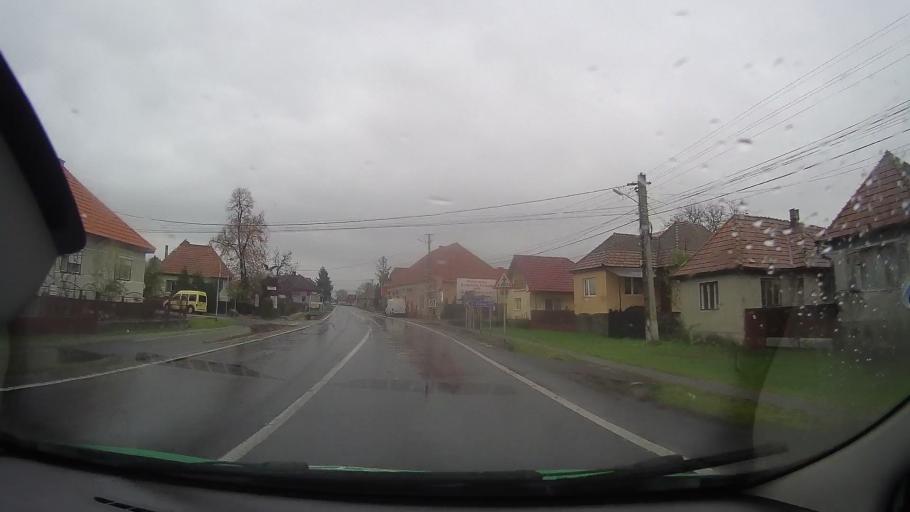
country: RO
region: Mures
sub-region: Comuna Brancovenesti
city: Valenii de Mures
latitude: 46.8907
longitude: 24.7976
